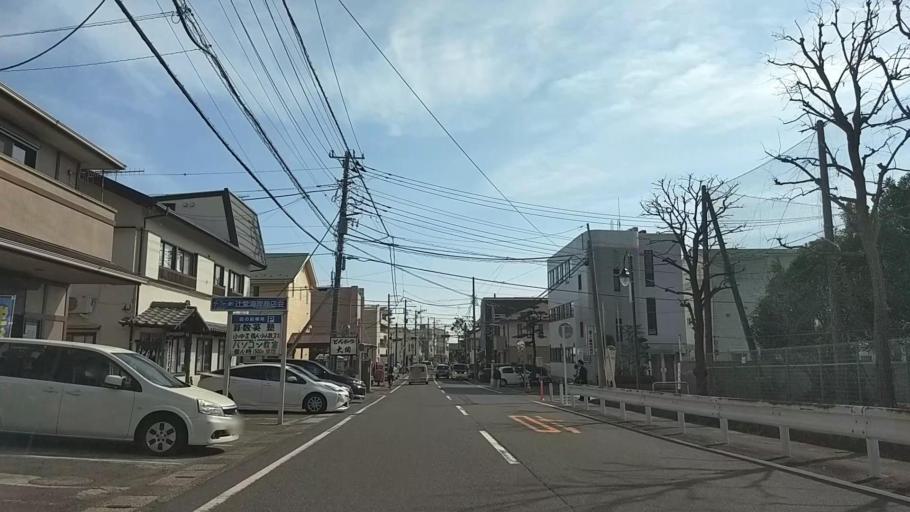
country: JP
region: Kanagawa
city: Fujisawa
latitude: 35.3249
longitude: 139.4536
